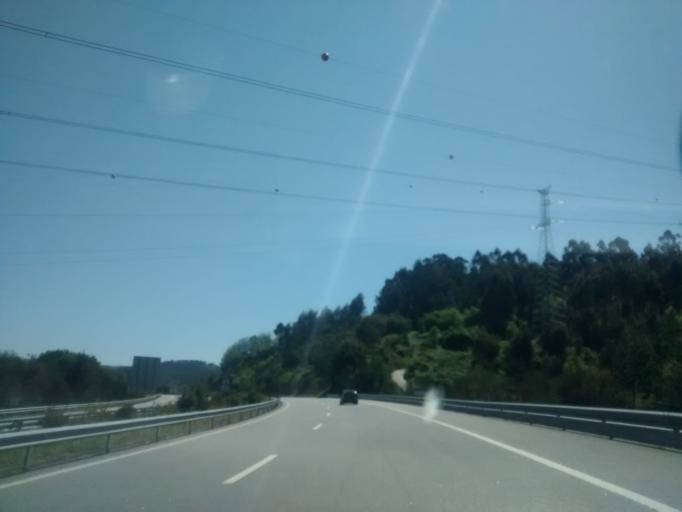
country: PT
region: Braga
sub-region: Guimaraes
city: Candoso
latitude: 41.4222
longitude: -8.3303
